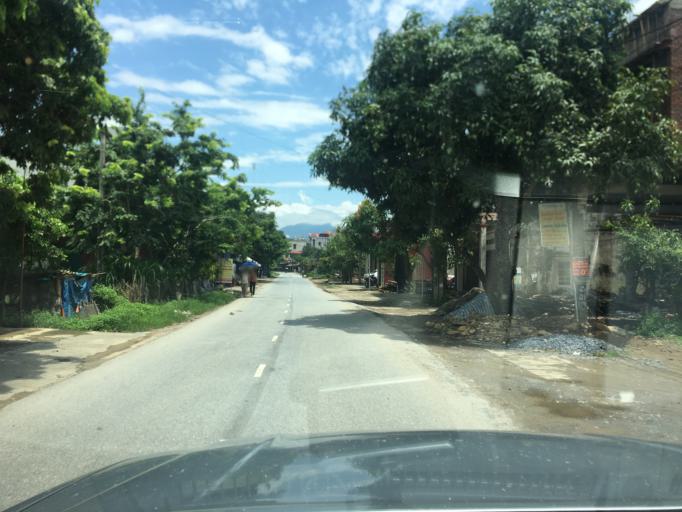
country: VN
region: Yen Bai
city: Son Thinh
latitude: 21.6419
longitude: 104.5007
